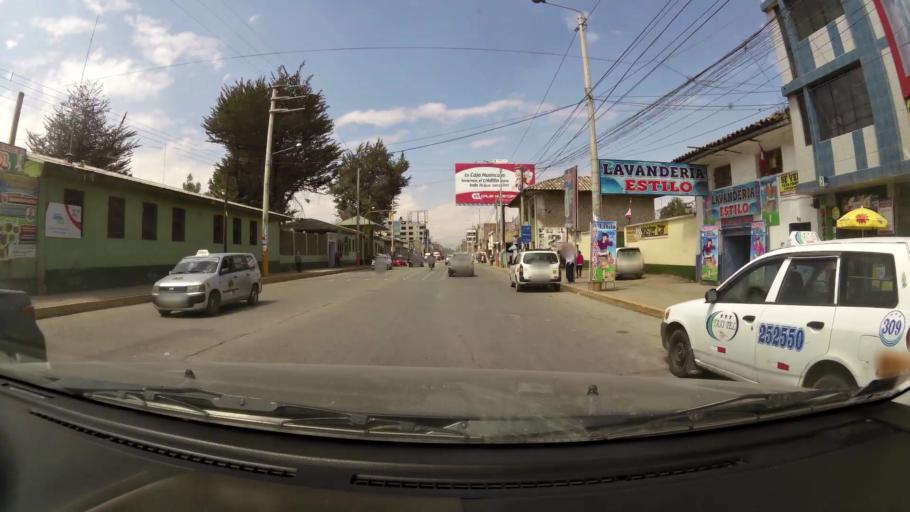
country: PE
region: Junin
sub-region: Provincia de Huancayo
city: Huancayo
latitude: -12.0819
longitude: -75.2021
